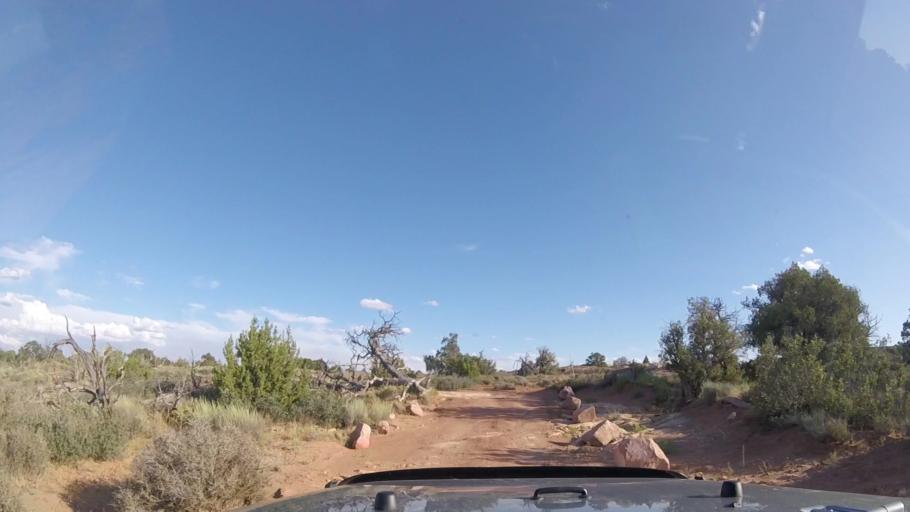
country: US
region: Utah
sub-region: Grand County
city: Moab
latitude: 38.2148
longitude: -109.8121
